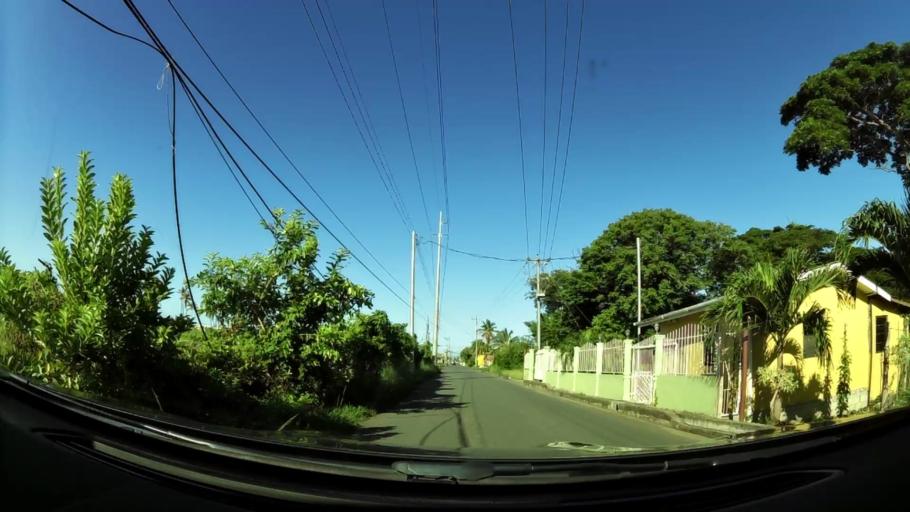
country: TT
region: Tobago
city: Scarborough
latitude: 11.1523
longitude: -60.8171
